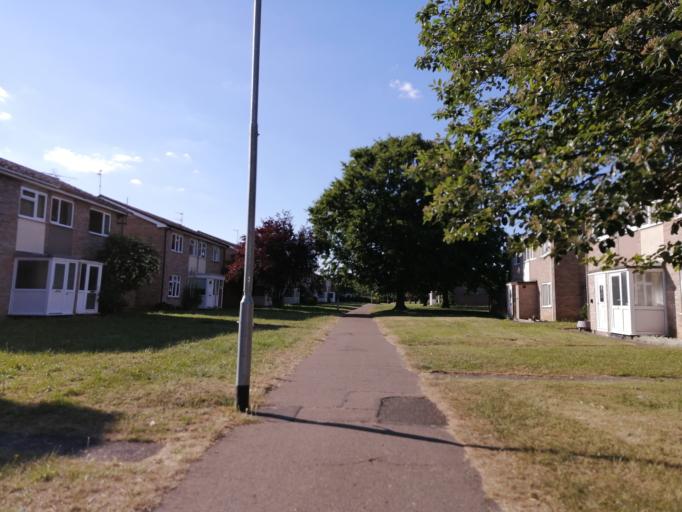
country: GB
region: England
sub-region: Peterborough
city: Peterborough
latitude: 52.5910
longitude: -0.2719
